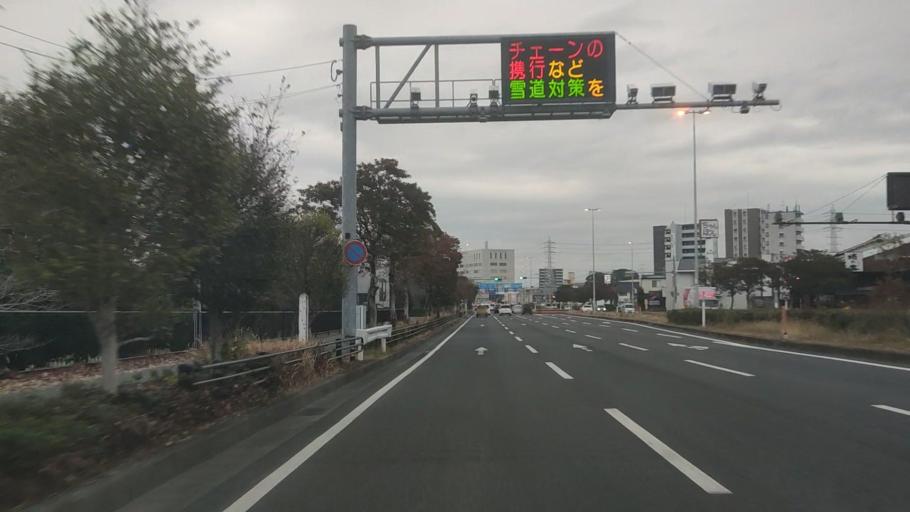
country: JP
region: Kumamoto
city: Kumamoto
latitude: 32.7781
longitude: 130.7410
